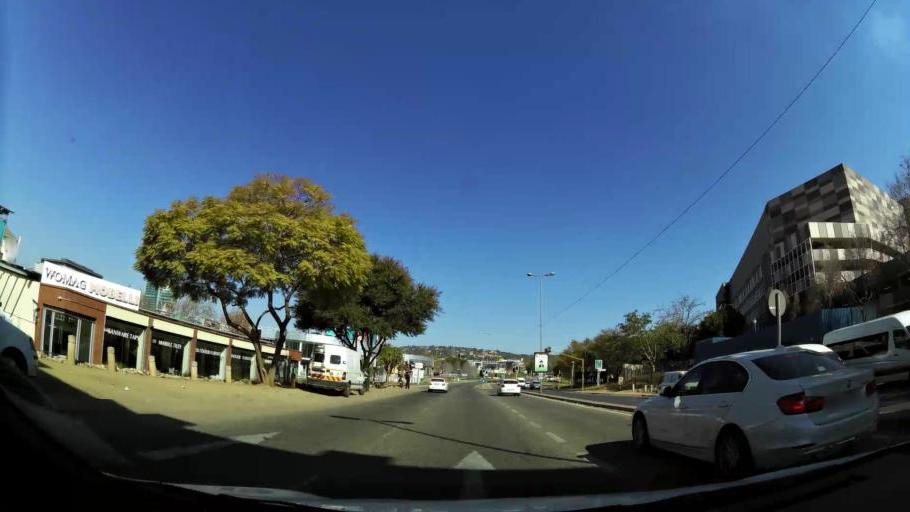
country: ZA
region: Gauteng
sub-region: City of Tshwane Metropolitan Municipality
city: Pretoria
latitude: -25.7837
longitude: 28.2775
